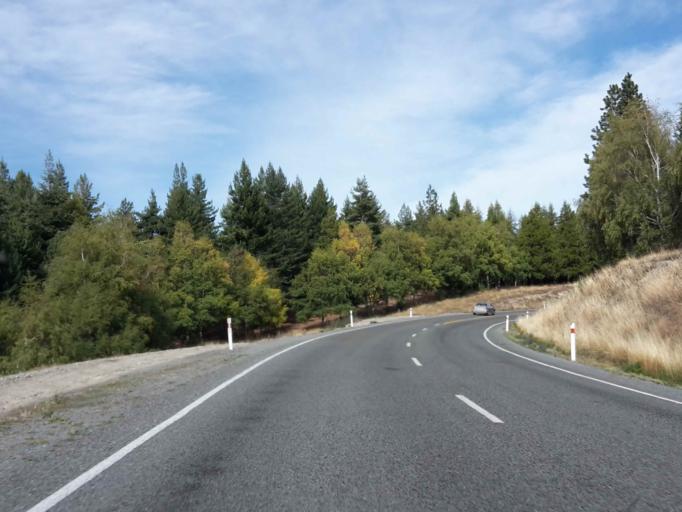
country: NZ
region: Canterbury
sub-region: Timaru District
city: Pleasant Point
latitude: -44.0117
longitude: 170.5003
